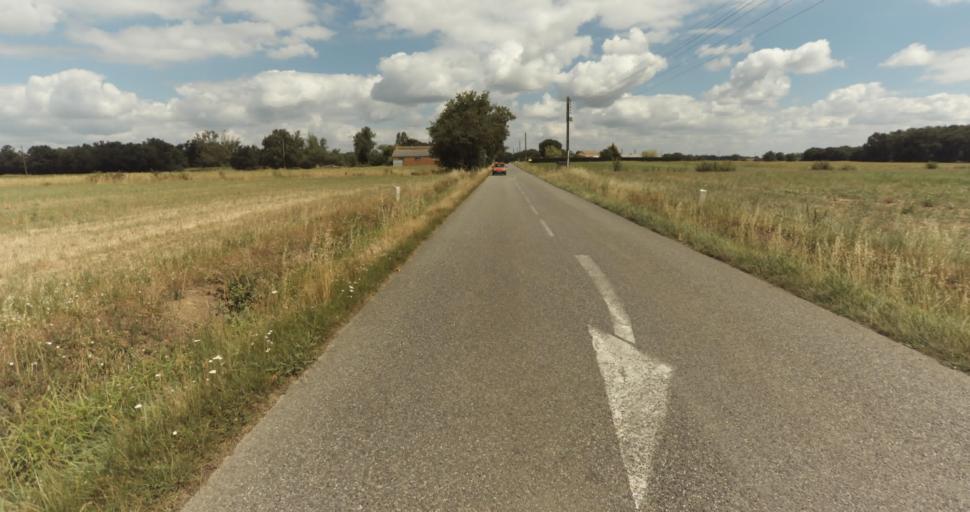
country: FR
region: Midi-Pyrenees
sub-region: Departement de la Haute-Garonne
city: Fontenilles
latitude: 43.5590
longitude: 1.1934
